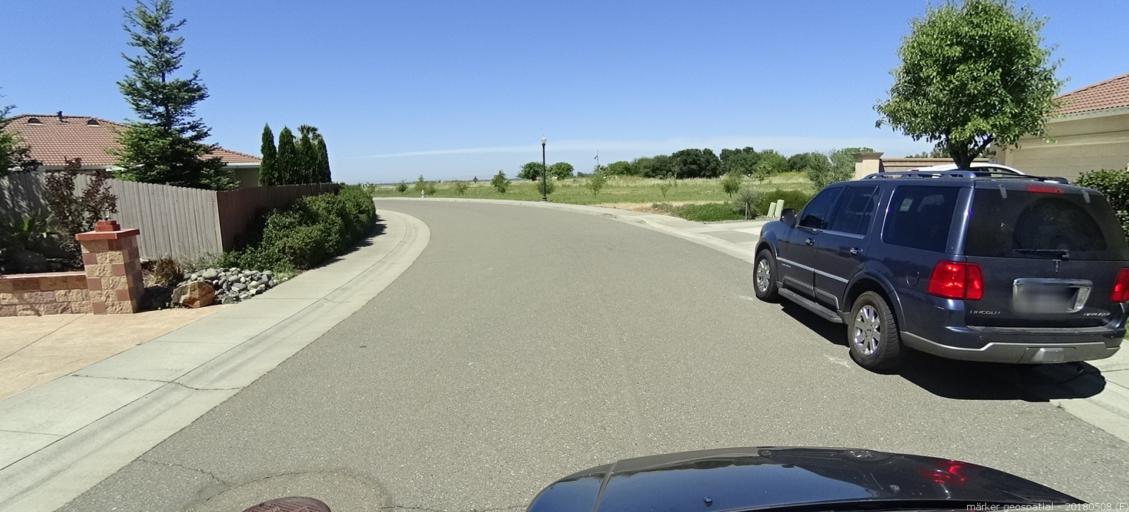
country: US
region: California
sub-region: Sacramento County
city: Elverta
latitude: 38.6838
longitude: -121.5377
